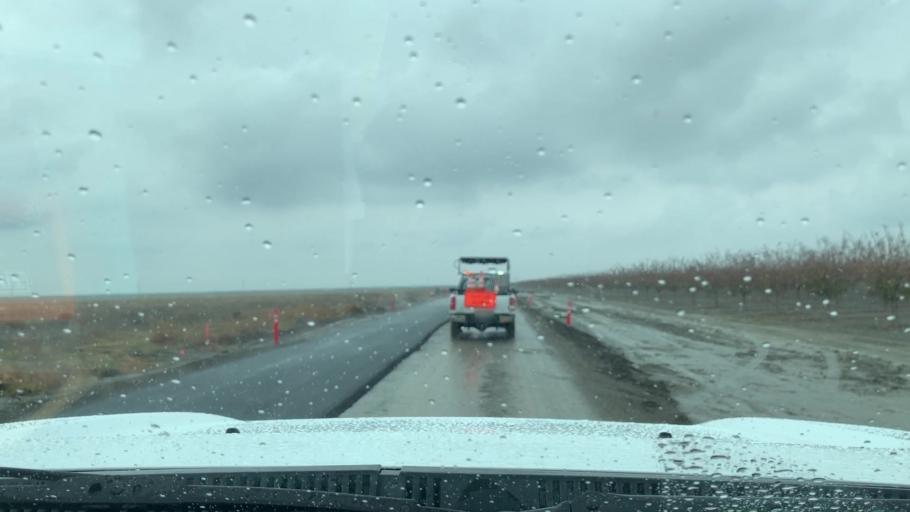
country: US
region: California
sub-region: Kings County
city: Corcoran
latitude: 36.0073
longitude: -119.4989
